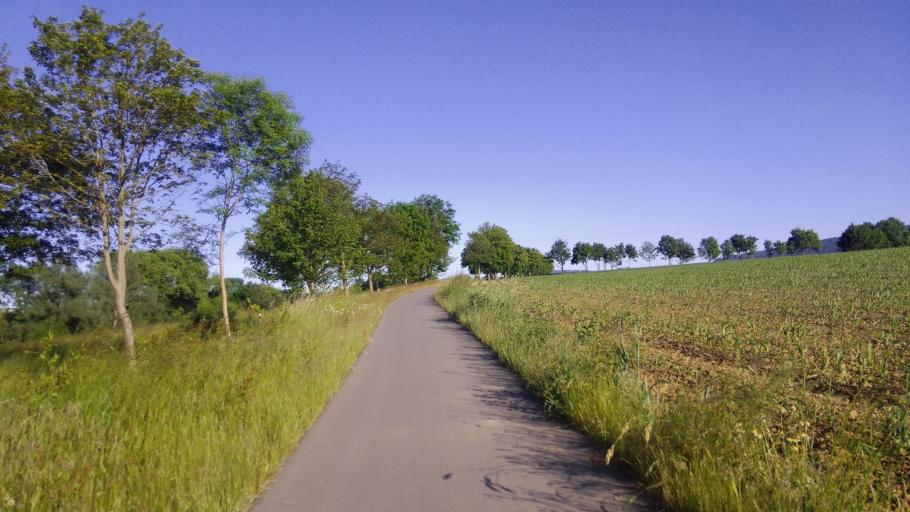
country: DE
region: Lower Saxony
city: Salzhemmendorf
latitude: 52.0348
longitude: 9.6075
